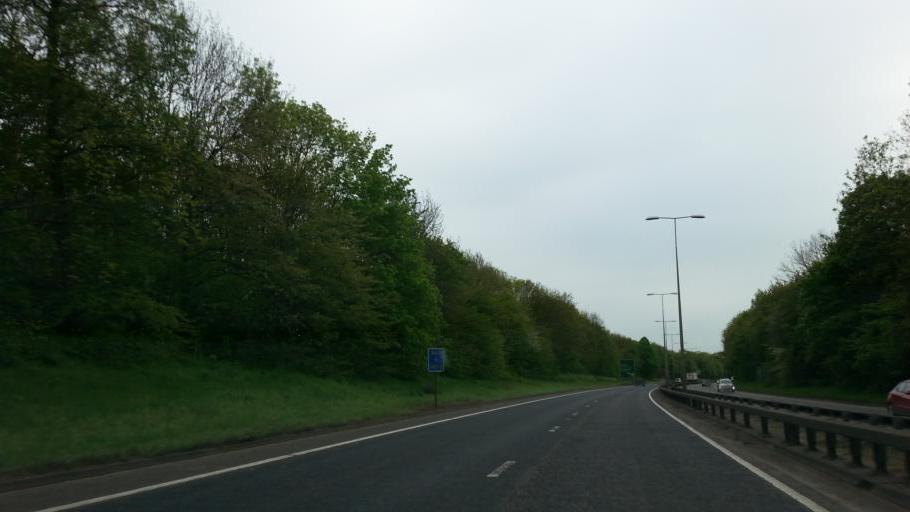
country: GB
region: England
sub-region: Peterborough
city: Marholm
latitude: 52.5825
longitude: -0.2815
